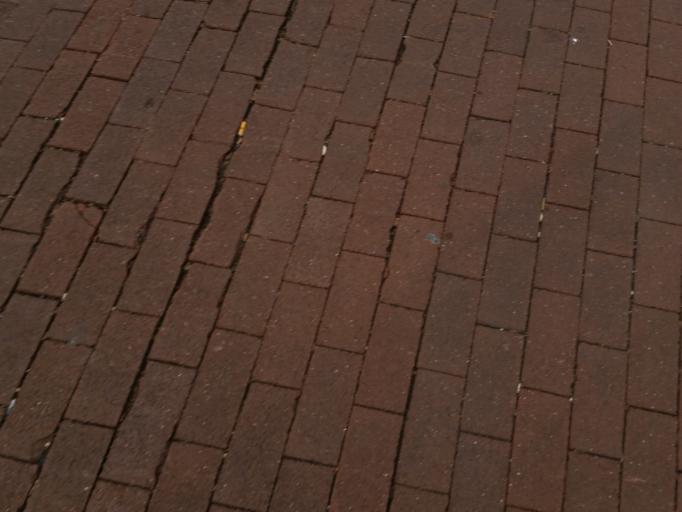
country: US
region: Washington, D.C.
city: Washington, D.C.
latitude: 38.9075
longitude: -77.0373
